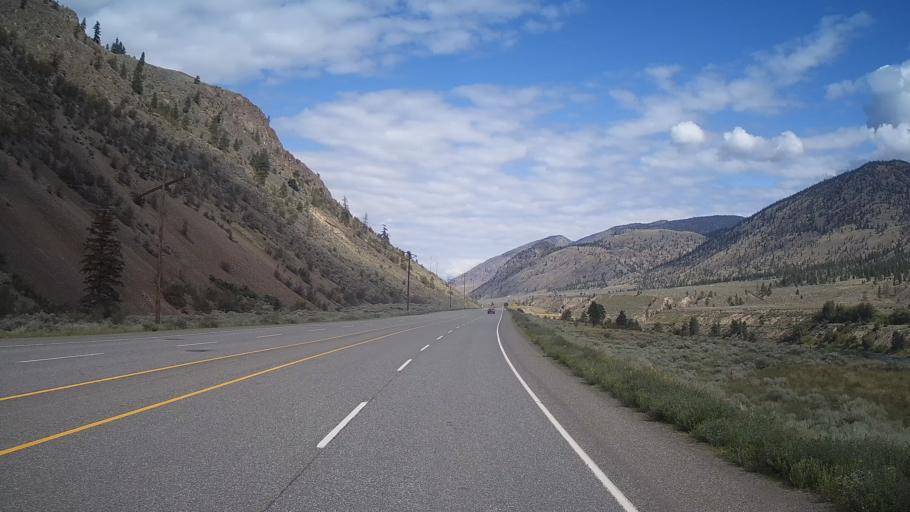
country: CA
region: British Columbia
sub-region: Thompson-Nicola Regional District
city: Ashcroft
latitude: 50.5235
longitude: -121.2856
